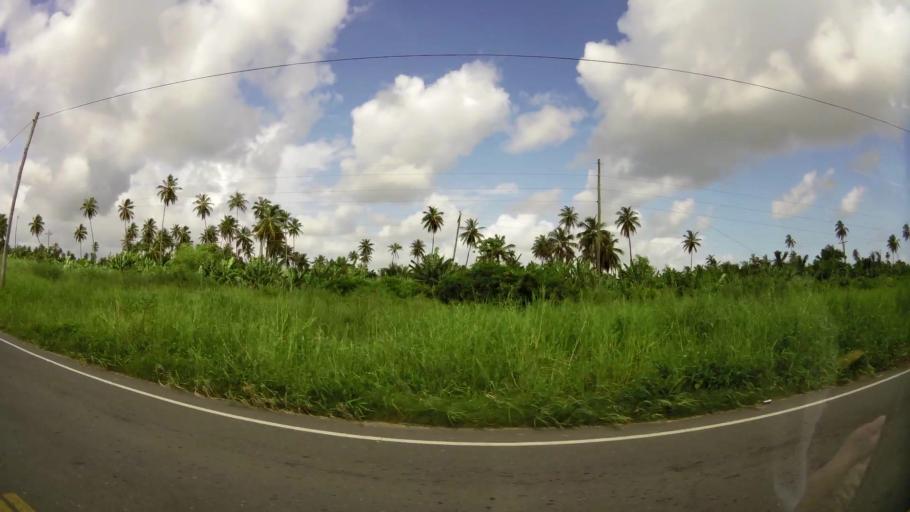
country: GY
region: Demerara-Mahaica
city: Mahaica Village
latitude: 6.7177
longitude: -57.9337
